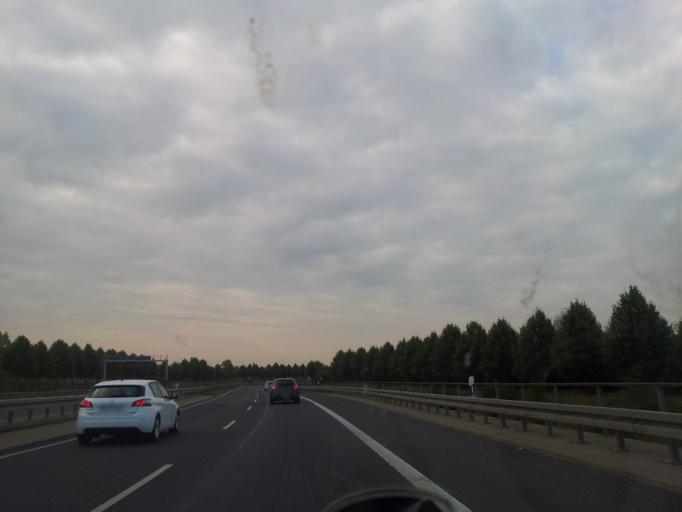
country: DE
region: Saxony
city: Rackwitz
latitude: 51.3941
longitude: 12.3912
